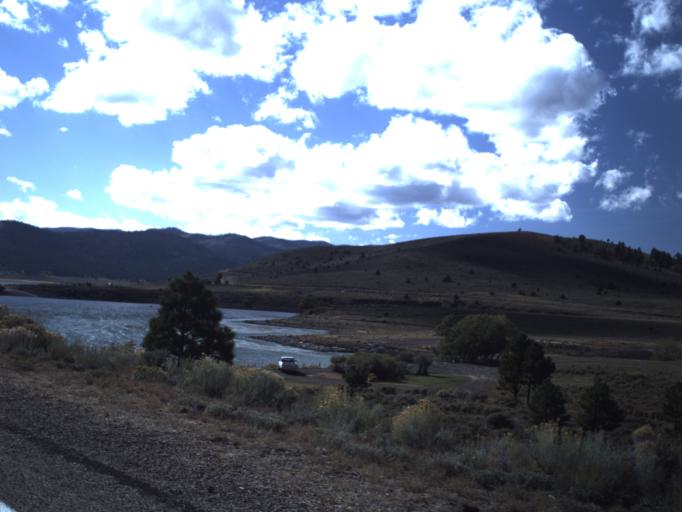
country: US
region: Utah
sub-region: Garfield County
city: Panguitch
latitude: 37.7233
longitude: -112.6252
